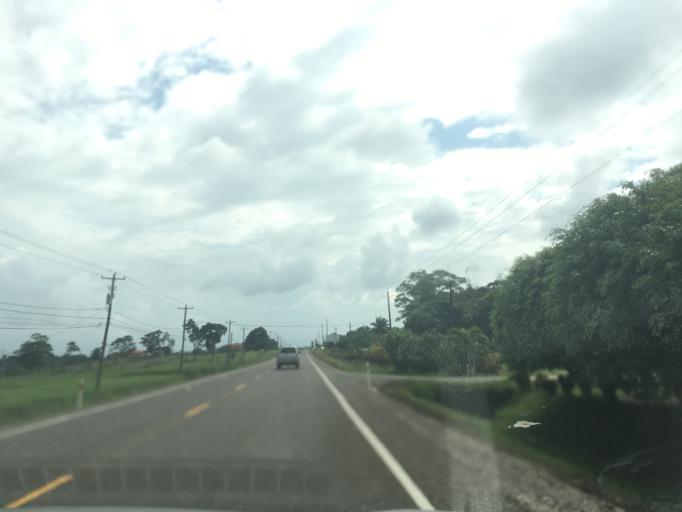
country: BZ
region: Stann Creek
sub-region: Dangriga
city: Dangriga
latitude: 16.9893
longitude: -88.2987
